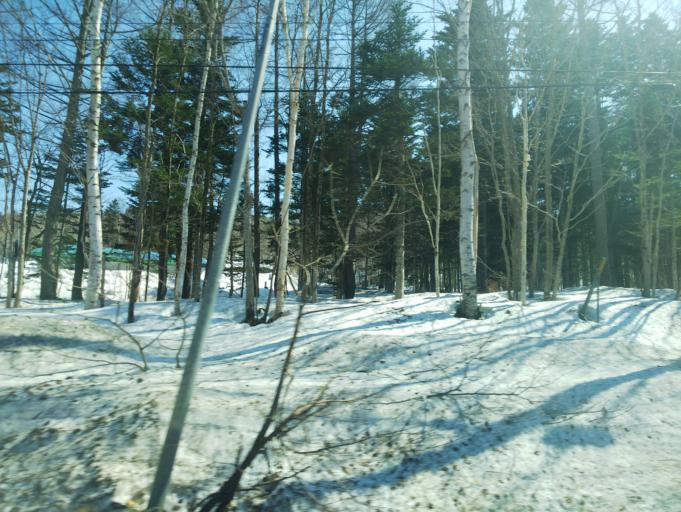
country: JP
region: Hokkaido
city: Nayoro
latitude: 44.7175
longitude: 142.2717
